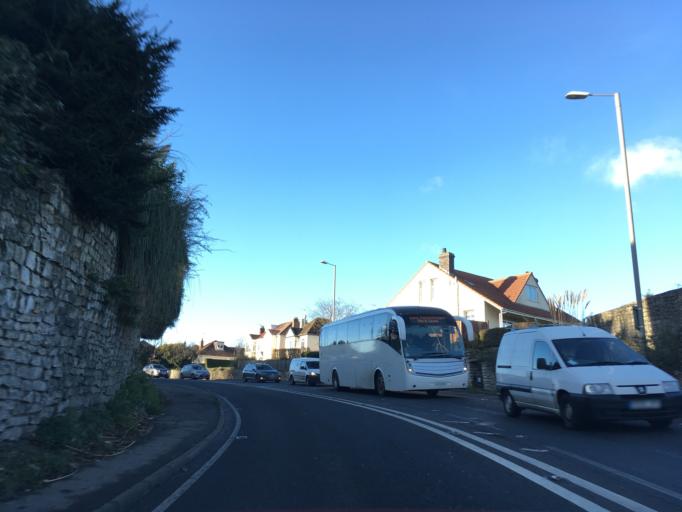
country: GB
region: England
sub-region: Bath and North East Somerset
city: Saltford
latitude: 51.4004
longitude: -2.4523
